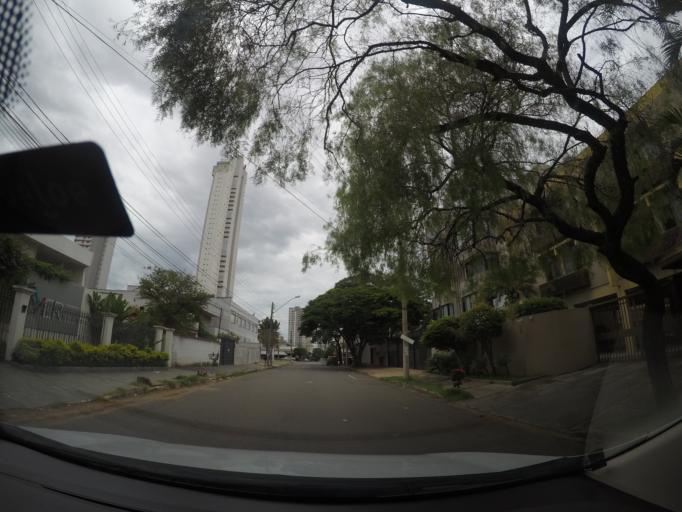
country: BR
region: Goias
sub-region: Goiania
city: Goiania
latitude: -16.7037
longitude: -49.2632
